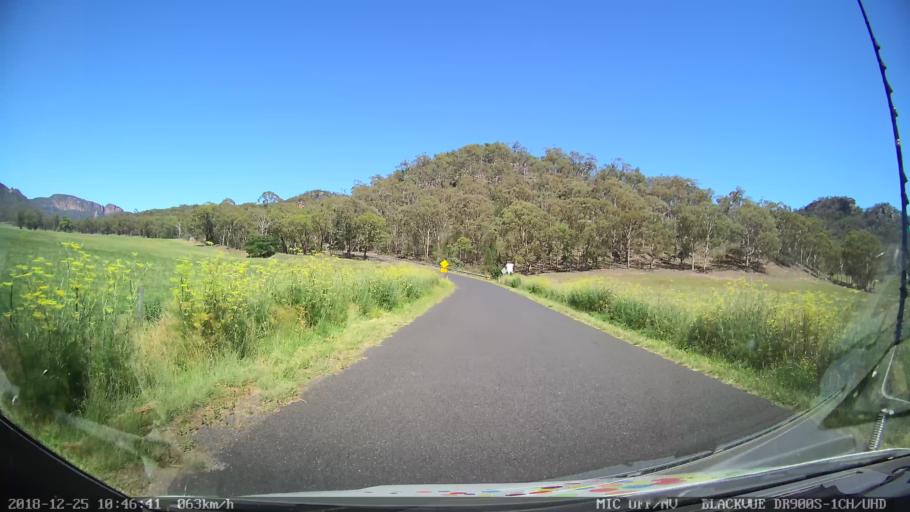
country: AU
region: New South Wales
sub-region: Upper Hunter Shire
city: Merriwa
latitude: -32.4441
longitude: 150.2827
